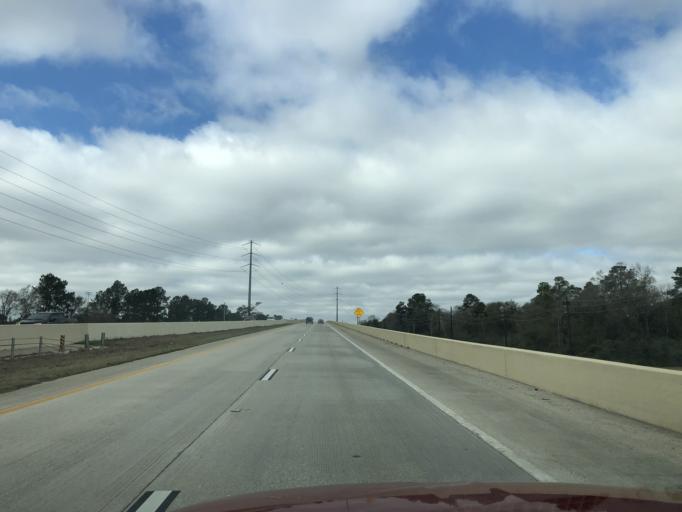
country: US
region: Texas
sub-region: Montgomery County
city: The Woodlands
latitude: 30.0944
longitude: -95.4868
